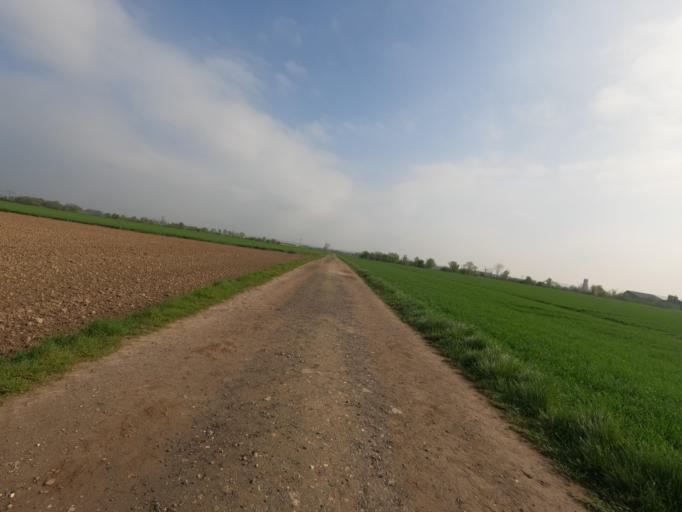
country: DE
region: North Rhine-Westphalia
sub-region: Regierungsbezirk Koln
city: Heinsberg
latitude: 51.0402
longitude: 6.1142
